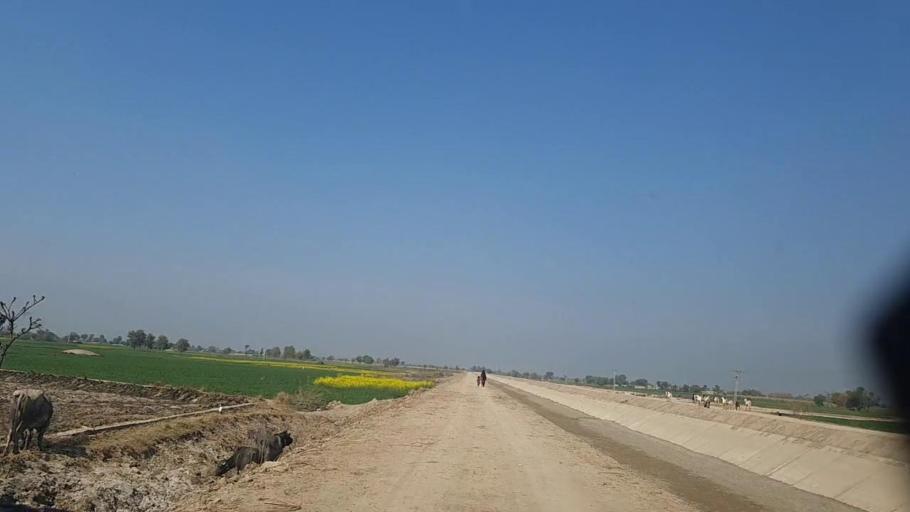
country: PK
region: Sindh
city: Sakrand
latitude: 26.1541
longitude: 68.3295
